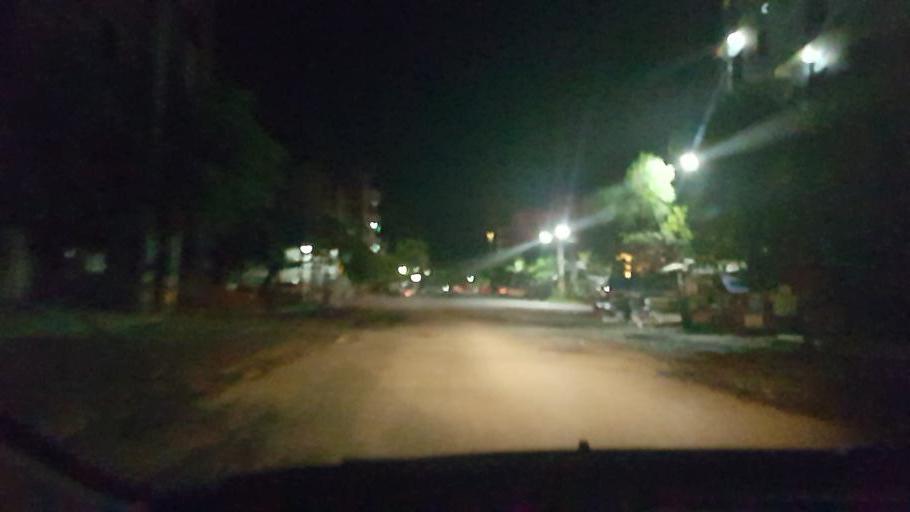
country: MM
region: Mandalay
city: Mandalay
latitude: 21.9813
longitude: 96.0914
